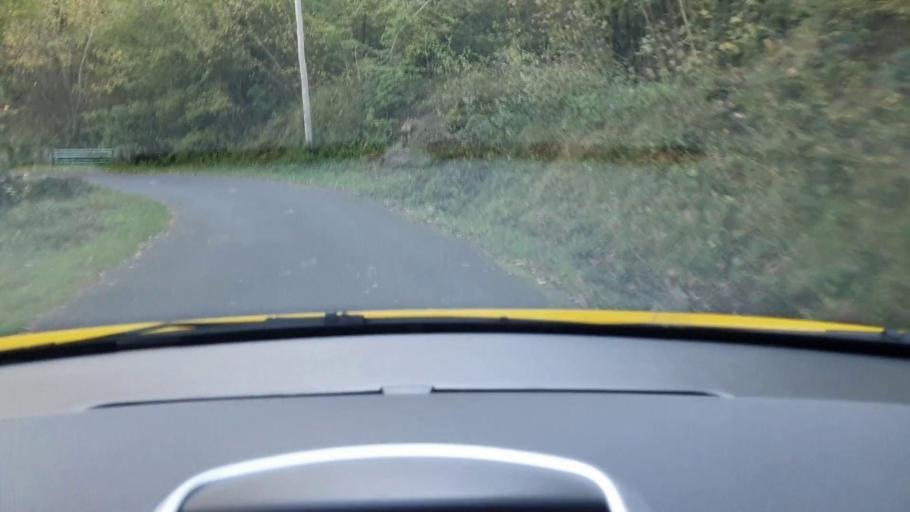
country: FR
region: Languedoc-Roussillon
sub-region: Departement du Gard
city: Sumene
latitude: 43.9839
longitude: 3.7440
